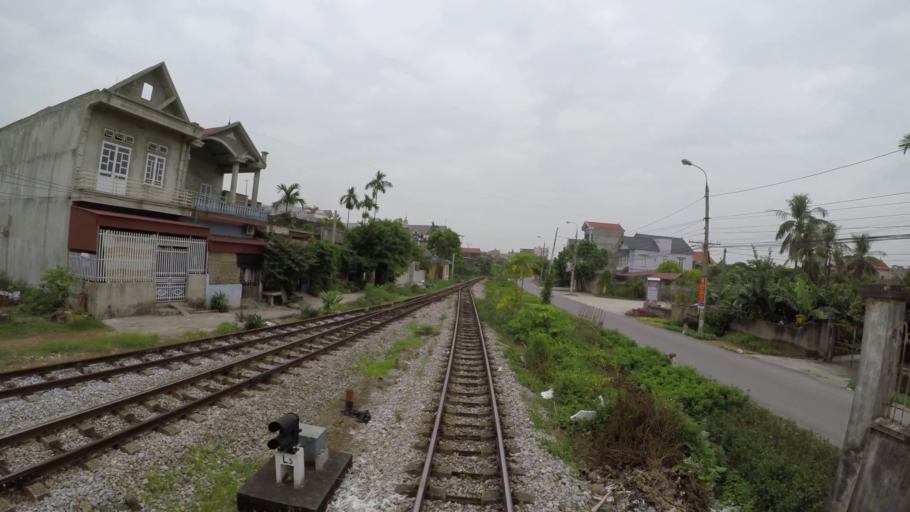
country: VN
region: Hai Duong
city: Phu Thai
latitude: 20.9686
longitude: 106.5011
